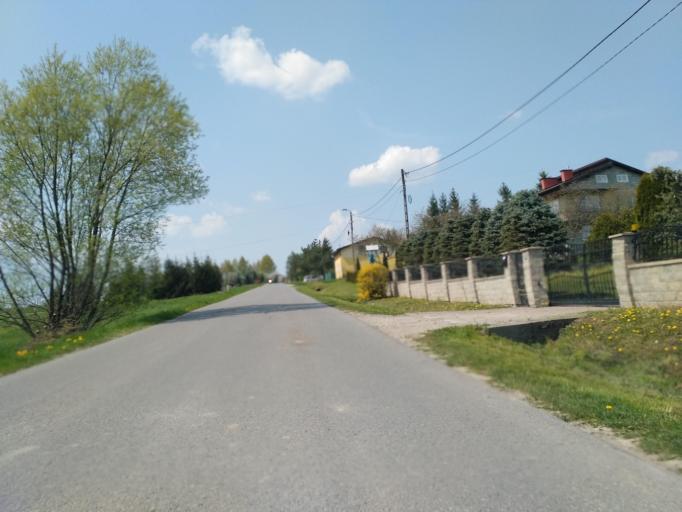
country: PL
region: Subcarpathian Voivodeship
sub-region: Powiat jasielski
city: Tarnowiec
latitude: 49.6708
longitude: 21.5526
